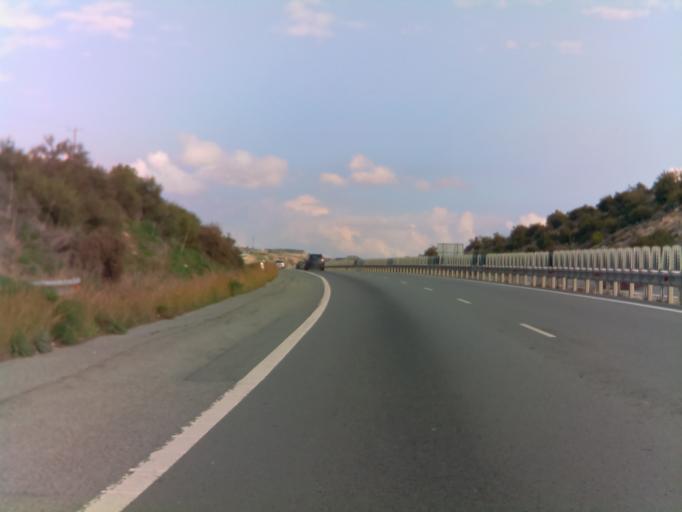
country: CY
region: Larnaka
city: Kofinou
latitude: 34.7821
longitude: 33.3440
